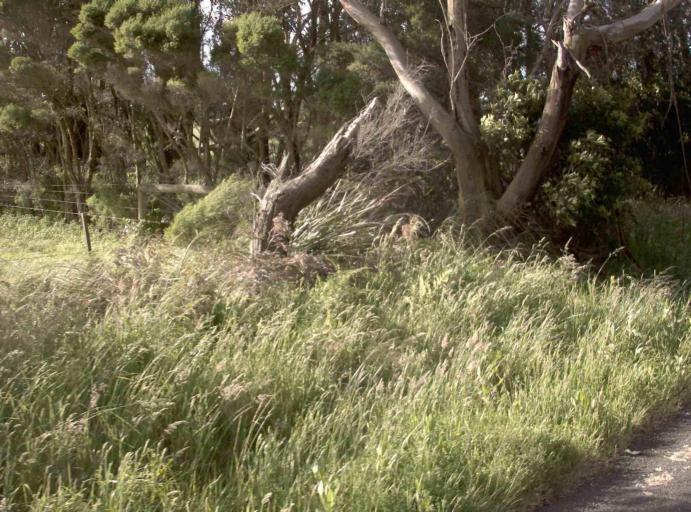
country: AU
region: Victoria
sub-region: Bass Coast
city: North Wonthaggi
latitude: -38.5573
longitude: 145.8434
